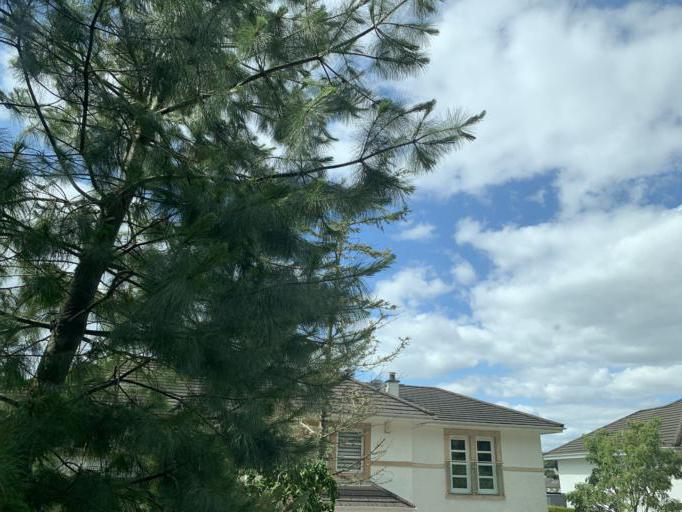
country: GB
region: Scotland
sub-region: East Renfrewshire
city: Newton Mearns
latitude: 55.7809
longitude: -4.3317
